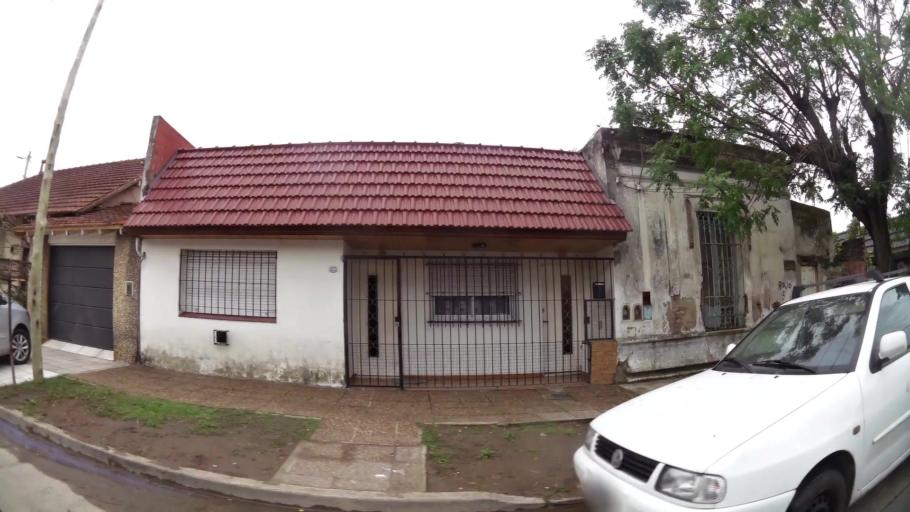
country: AR
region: Buenos Aires
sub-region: Partido de Lanus
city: Lanus
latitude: -34.7361
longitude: -58.3749
